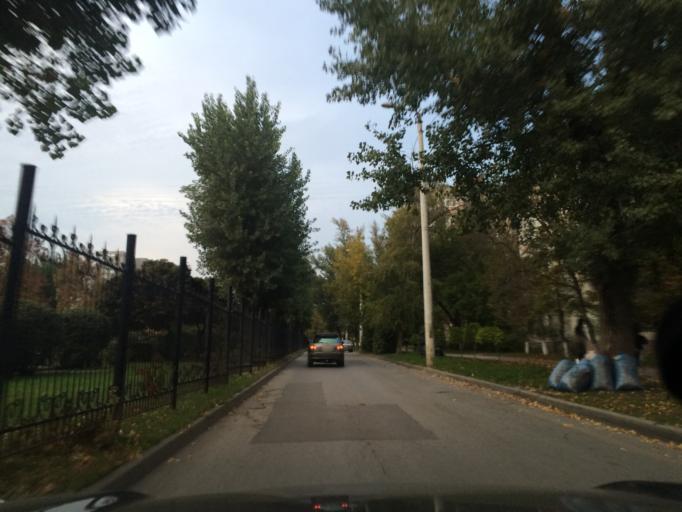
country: RU
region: Rostov
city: Rostov-na-Donu
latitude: 47.2063
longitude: 39.6339
